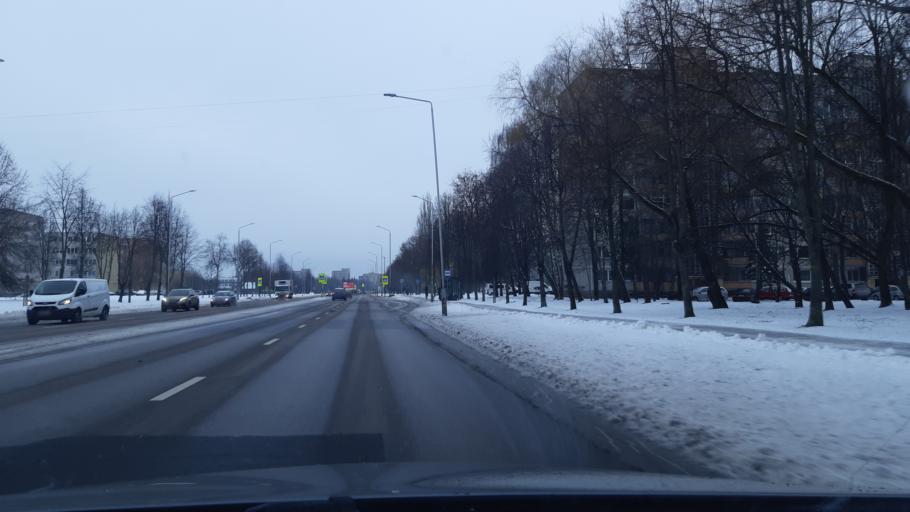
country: LT
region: Kauno apskritis
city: Dainava (Kaunas)
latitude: 54.9258
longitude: 23.9755
